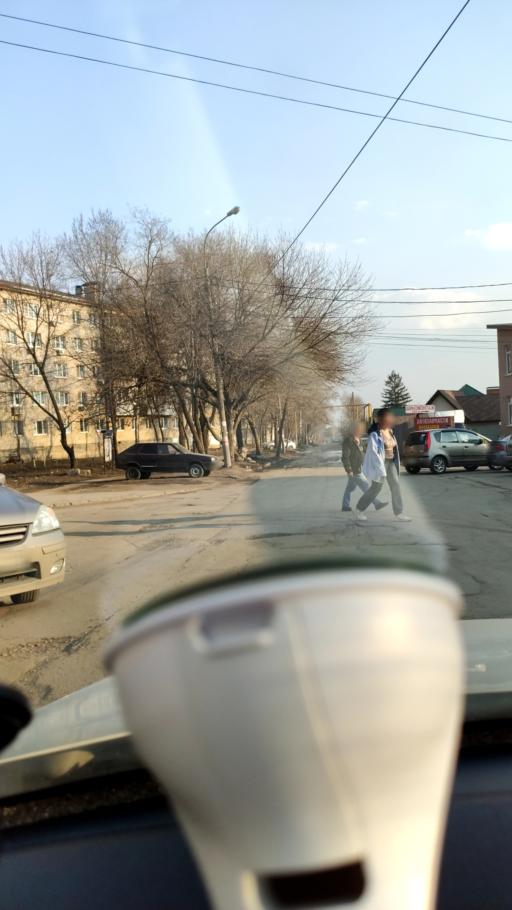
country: RU
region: Samara
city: Petra-Dubrava
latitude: 53.2988
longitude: 50.2775
